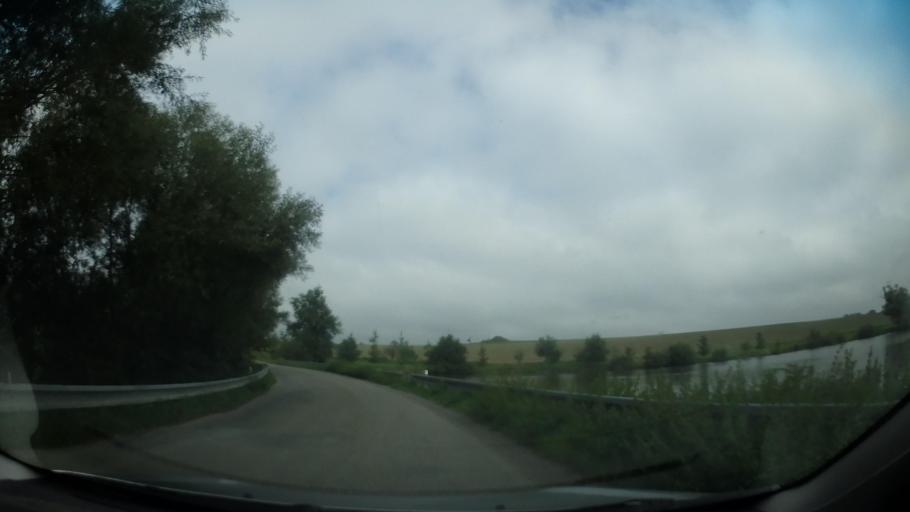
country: CZ
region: Central Bohemia
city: Sedlcany
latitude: 49.6997
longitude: 14.4380
